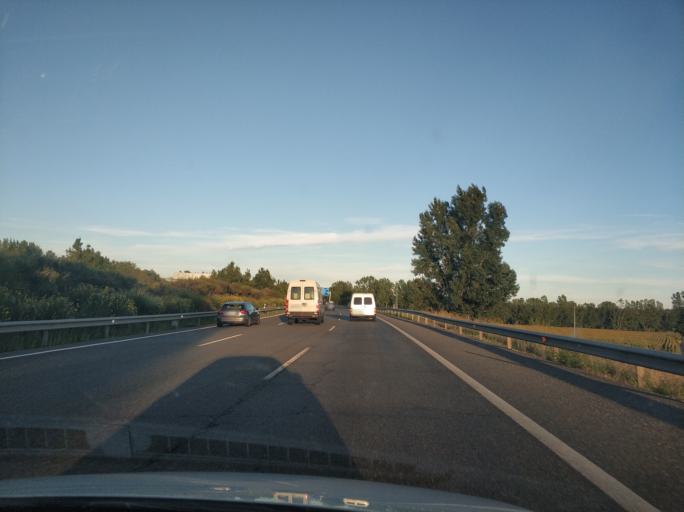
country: ES
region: Castille and Leon
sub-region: Provincia de Zamora
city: Castrogonzalo
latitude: 41.9858
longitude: -5.6323
